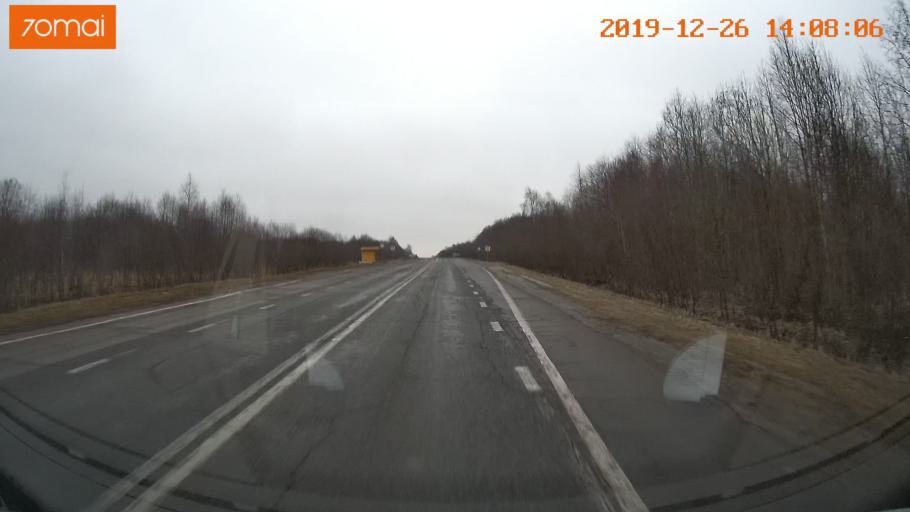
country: RU
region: Jaroslavl
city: Poshekhon'ye
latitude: 58.5087
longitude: 38.9049
